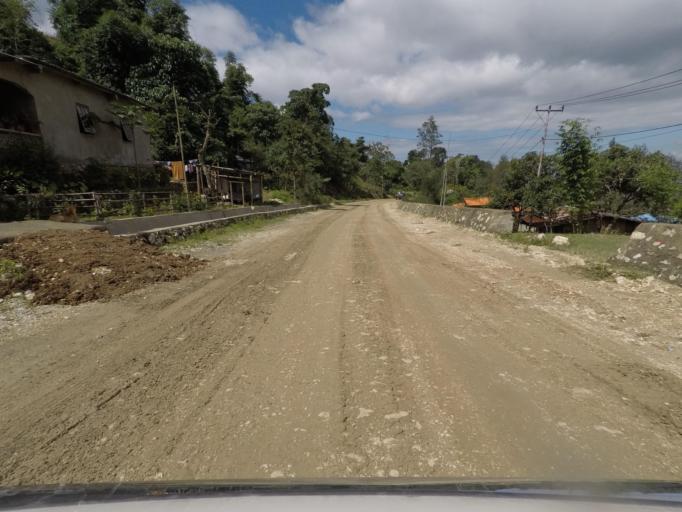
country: TL
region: Baucau
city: Venilale
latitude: -8.7284
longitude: 126.3694
